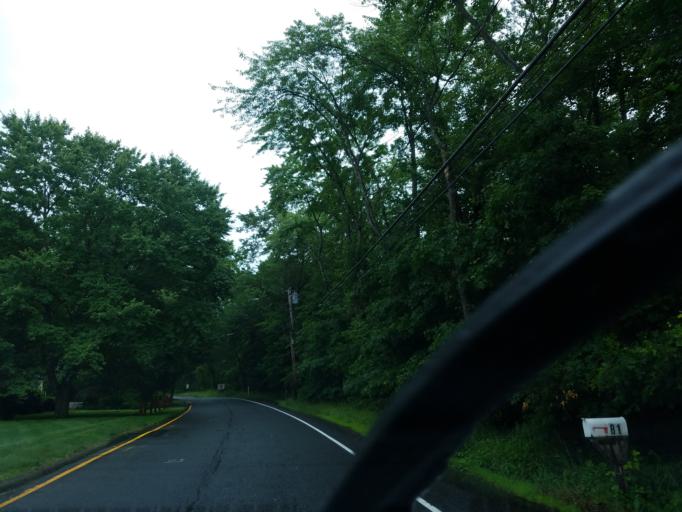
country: US
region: Connecticut
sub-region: Hartford County
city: Plainville
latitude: 41.6466
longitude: -72.8752
